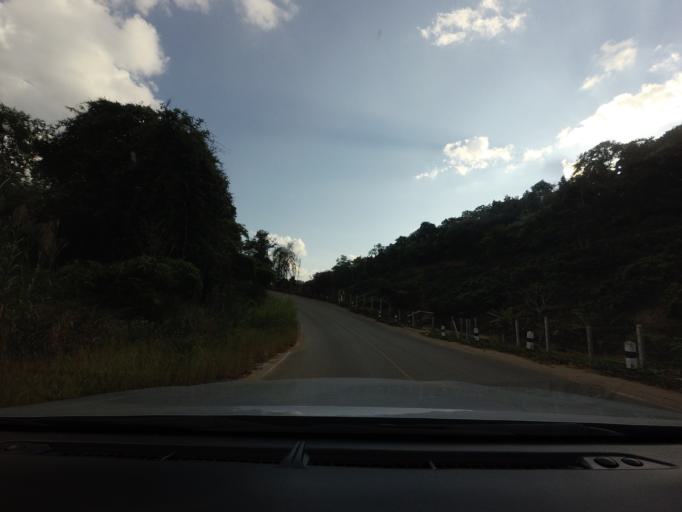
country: TH
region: Chiang Mai
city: Chai Prakan
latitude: 19.6409
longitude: 99.1616
